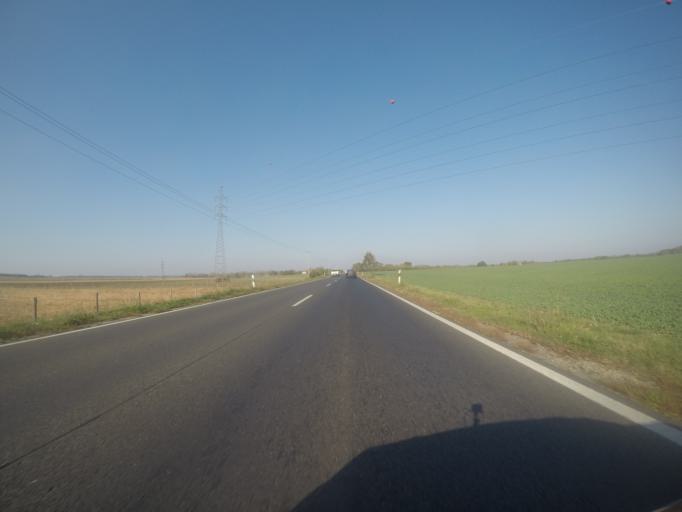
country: HU
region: Fejer
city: Baracs
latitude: 46.8458
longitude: 18.9109
